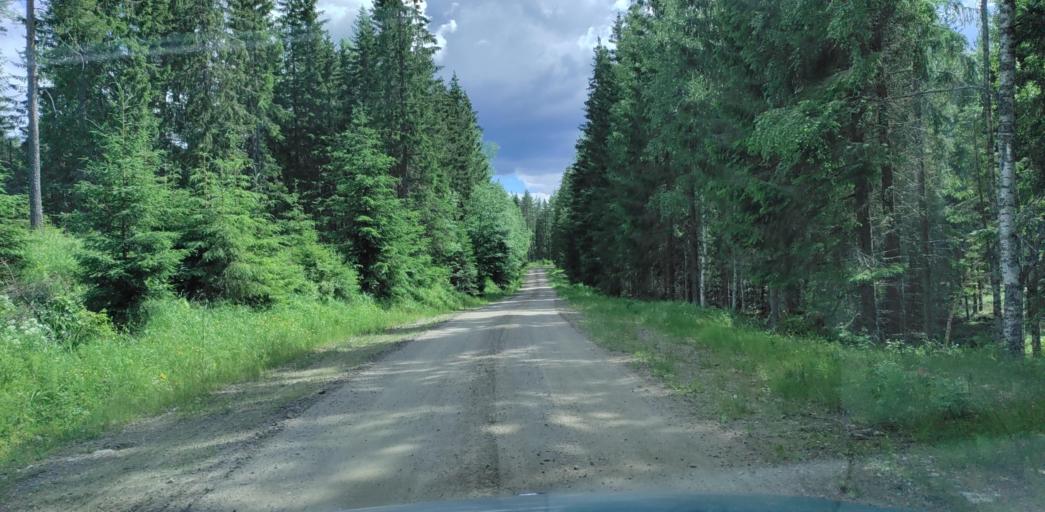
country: SE
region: Vaermland
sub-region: Hagfors Kommun
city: Ekshaerad
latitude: 60.0603
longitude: 13.3092
